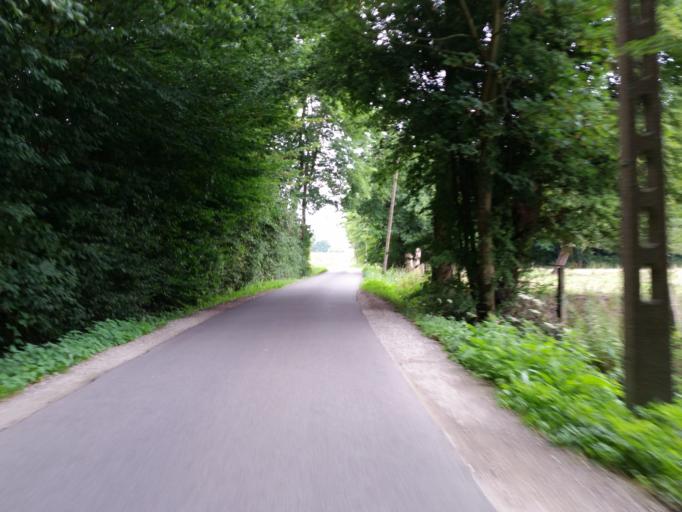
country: BE
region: Flanders
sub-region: Provincie Vlaams-Brabant
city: Zemst
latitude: 50.9870
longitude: 4.4427
